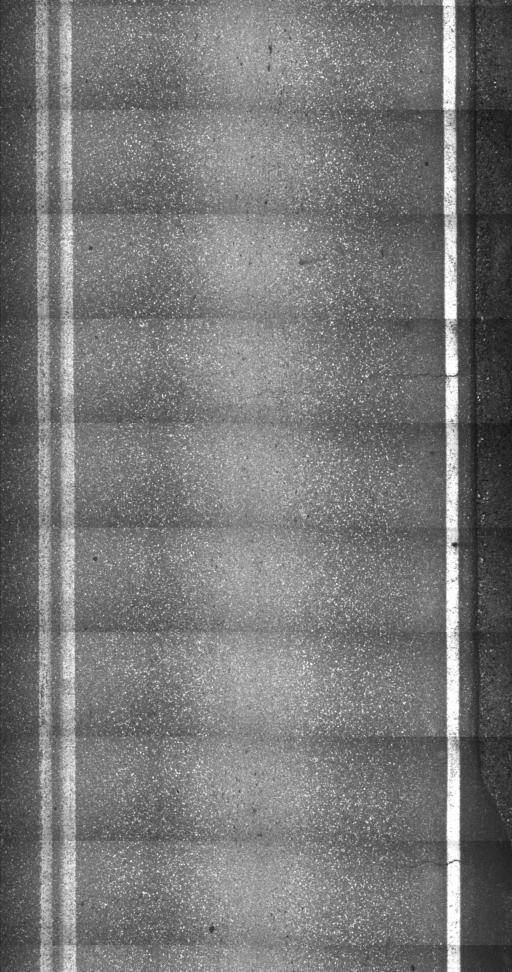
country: US
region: Vermont
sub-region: Orange County
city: Randolph
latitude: 43.8174
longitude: -72.5450
